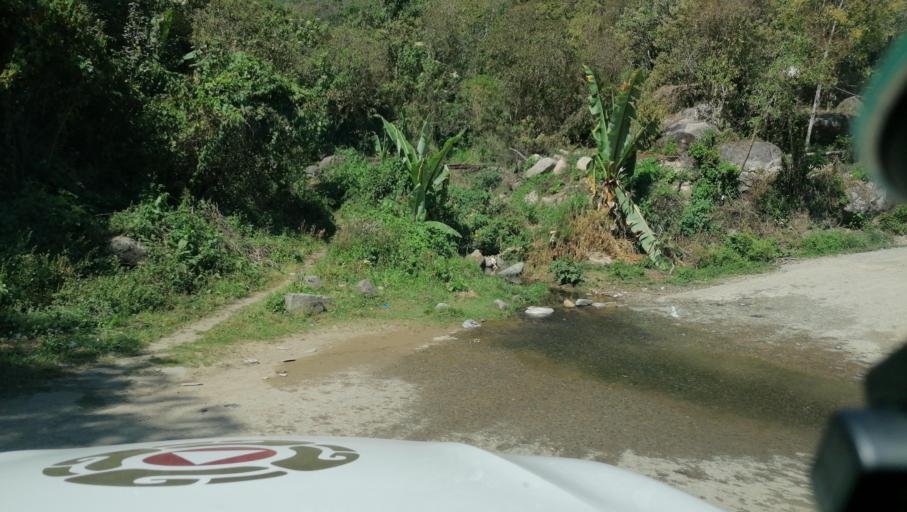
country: GT
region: San Marcos
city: Tacana
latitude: 15.2022
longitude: -92.1974
